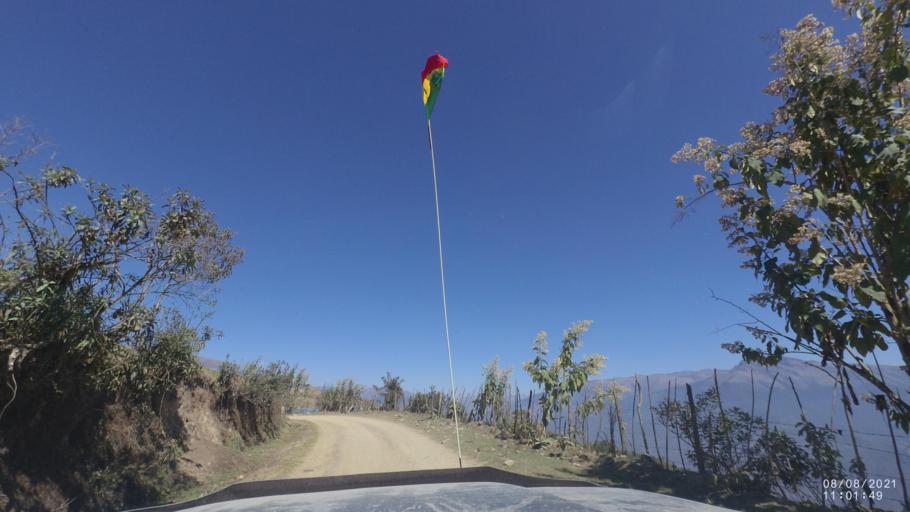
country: BO
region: Cochabamba
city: Colchani
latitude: -16.7514
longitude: -66.6867
